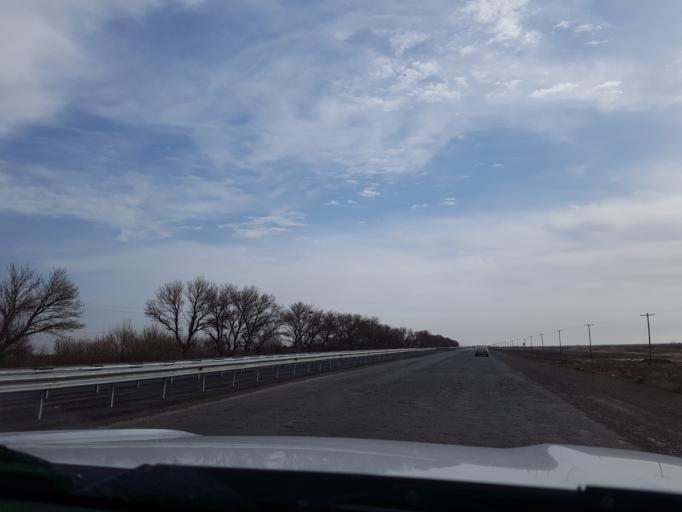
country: TM
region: Ahal
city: Tejen
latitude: 37.2288
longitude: 61.0172
